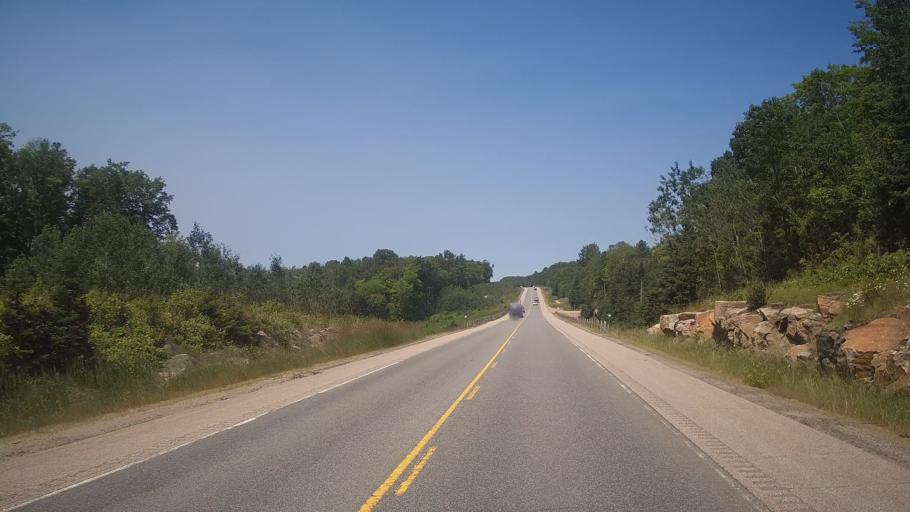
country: CA
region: Ontario
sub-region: Parry Sound District
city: Parry Sound
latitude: 45.4752
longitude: -80.1758
